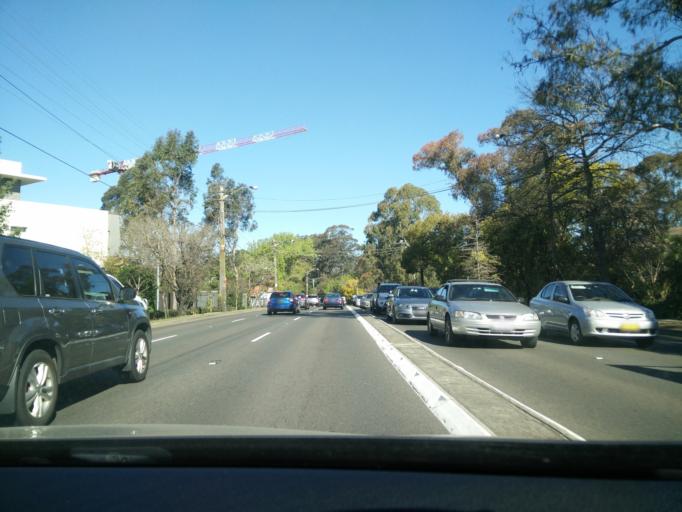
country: AU
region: New South Wales
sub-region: City of Sydney
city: Pymble
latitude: -33.7351
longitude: 151.1325
